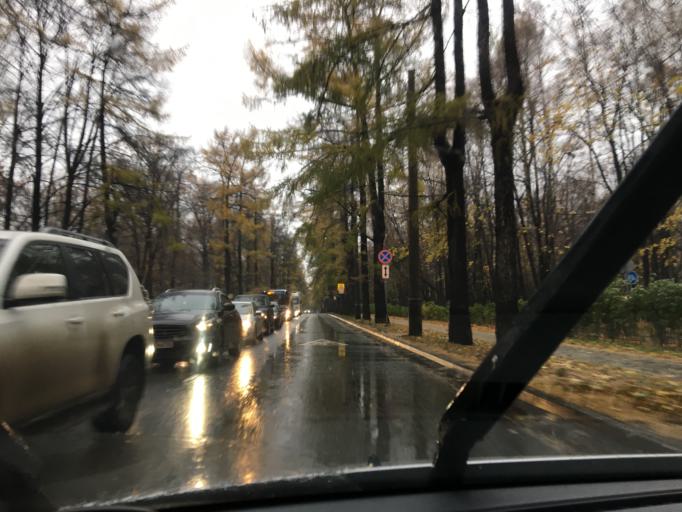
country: RU
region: Moscow
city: Sokol'niki
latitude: 55.7937
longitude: 37.6587
